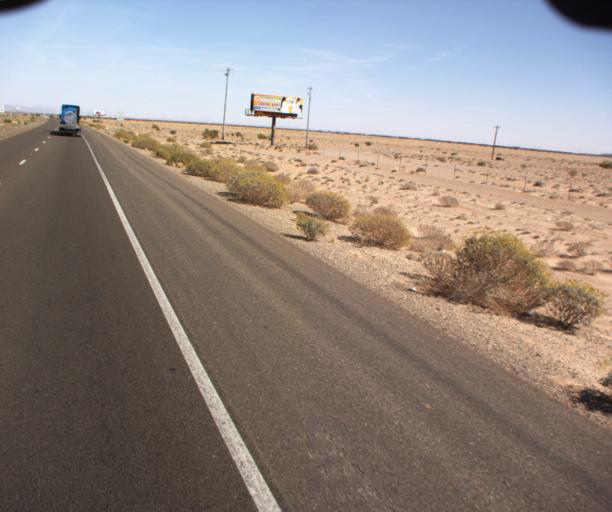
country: MX
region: Sonora
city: San Luis Rio Colorado
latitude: 32.4946
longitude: -114.6934
